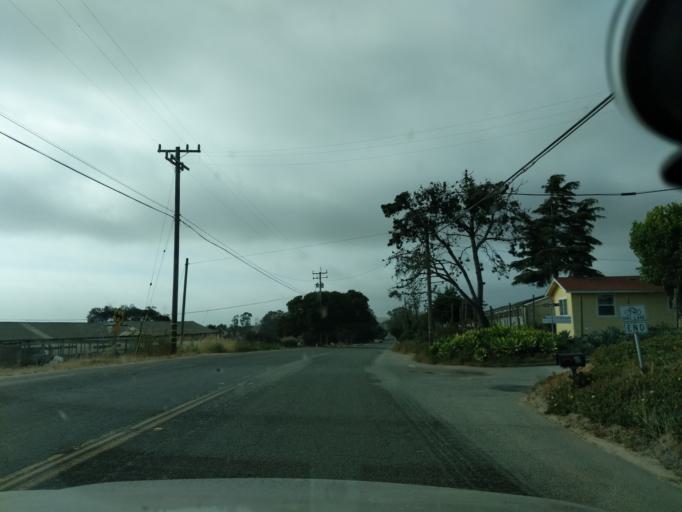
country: US
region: California
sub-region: Monterey County
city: Elkhorn
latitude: 36.8014
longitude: -121.7218
